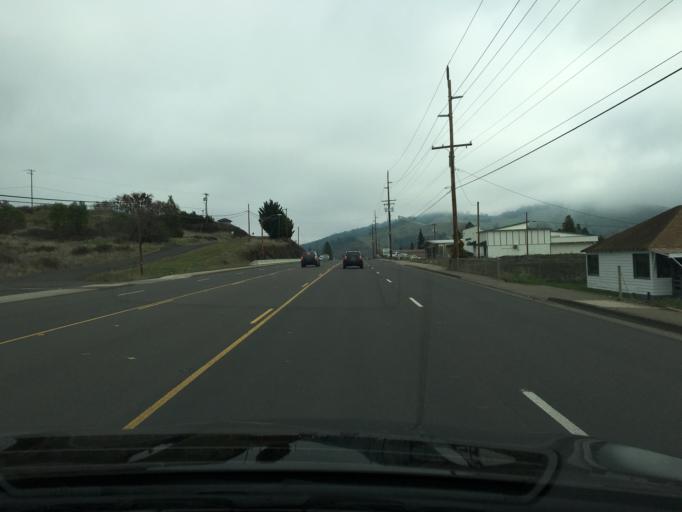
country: US
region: Oregon
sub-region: Douglas County
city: Roseburg
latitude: 43.2130
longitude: -123.3157
